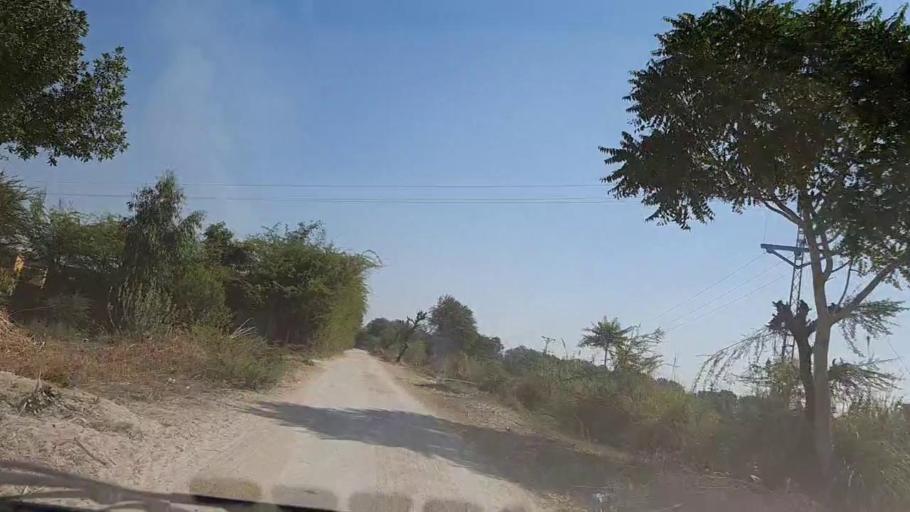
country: PK
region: Sindh
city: Mirpur Khas
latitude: 25.4303
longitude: 69.0219
